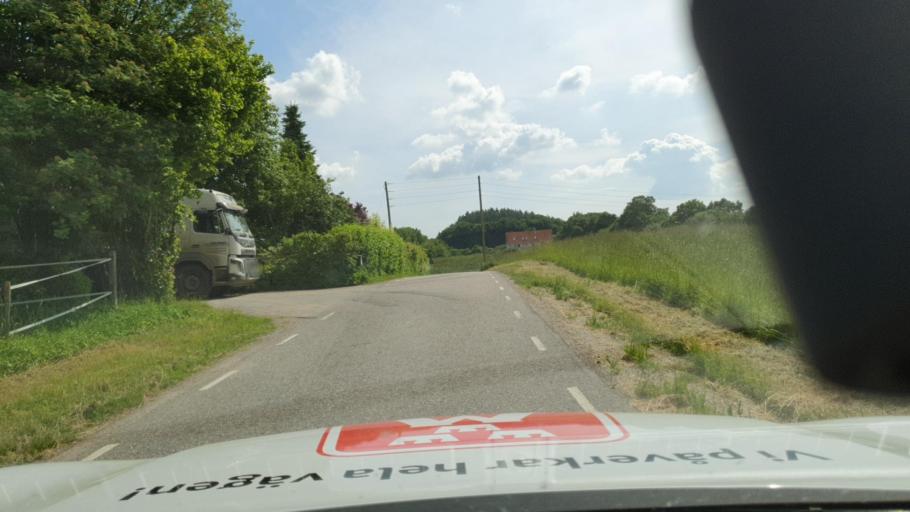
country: SE
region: Skane
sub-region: Skurups Kommun
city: Skurup
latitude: 55.5235
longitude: 13.4546
